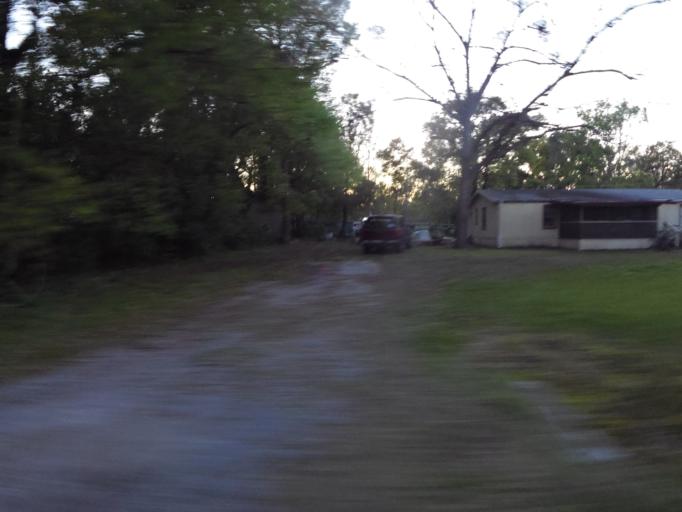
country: US
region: Florida
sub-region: Duval County
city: Jacksonville
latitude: 30.2739
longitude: -81.6308
